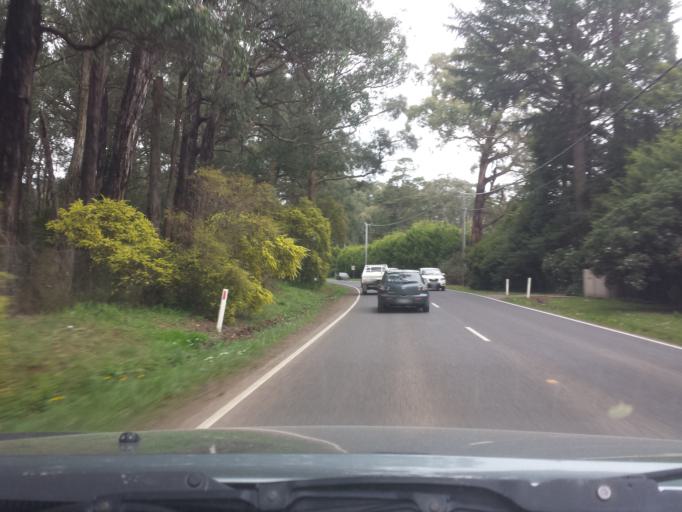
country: AU
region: Victoria
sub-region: Yarra Ranges
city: Monbulk
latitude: -37.8395
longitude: 145.4266
